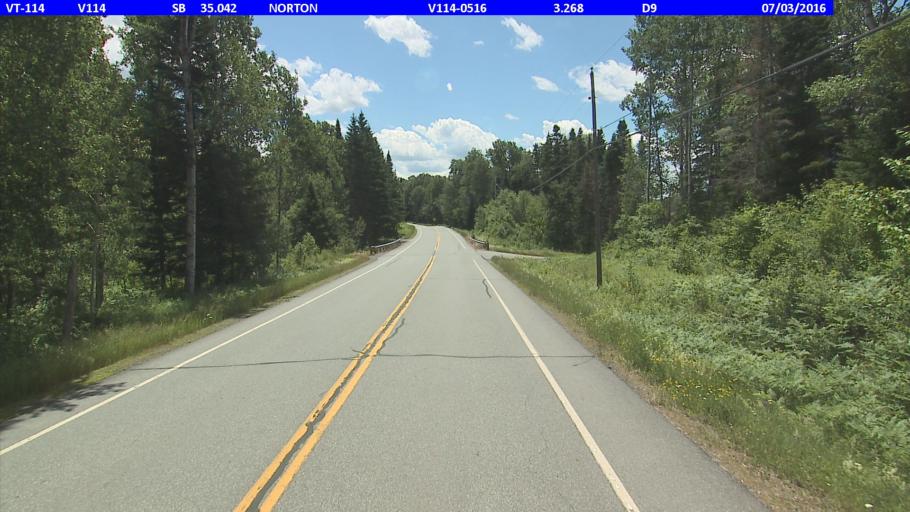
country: CA
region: Quebec
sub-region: Estrie
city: Coaticook
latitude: 44.9828
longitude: -71.8159
